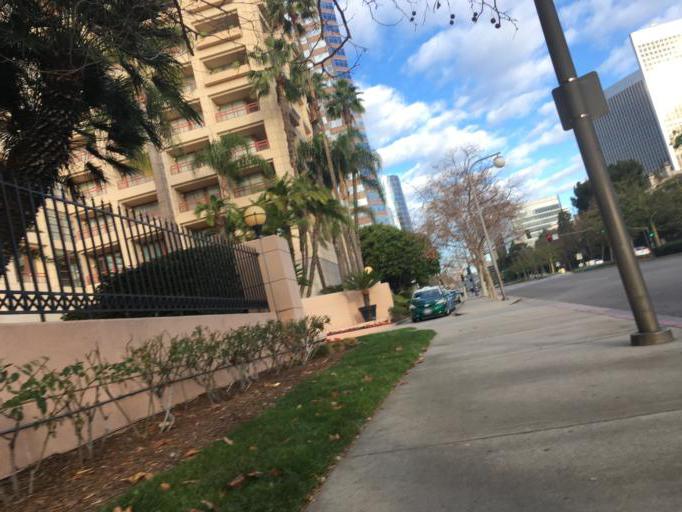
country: US
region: California
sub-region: Los Angeles County
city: Century City
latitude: 34.0542
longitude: -118.4119
